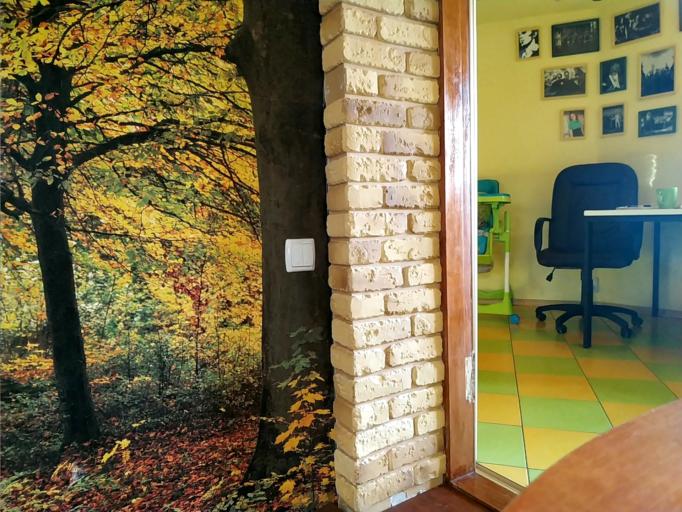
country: RU
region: Jaroslavl
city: Krasnyy Profintern
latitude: 57.9603
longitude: 40.5242
